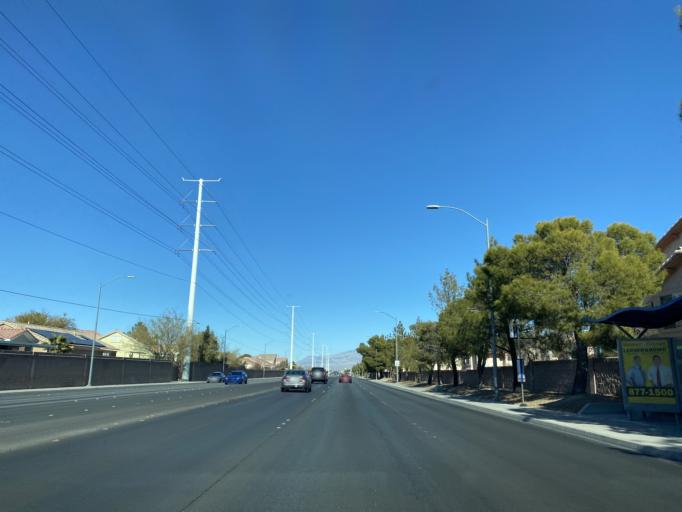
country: US
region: Nevada
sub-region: Clark County
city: Spring Valley
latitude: 36.1667
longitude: -115.2779
